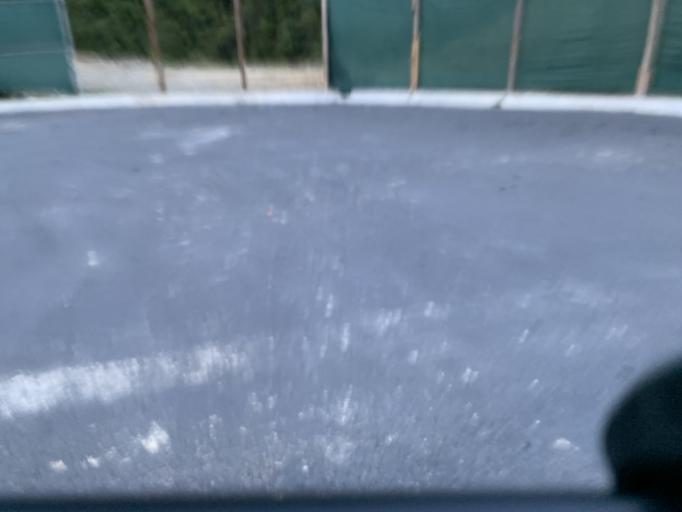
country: MX
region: Nuevo Leon
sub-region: Juarez
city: Bosques de San Pedro
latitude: 25.5242
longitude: -100.1901
